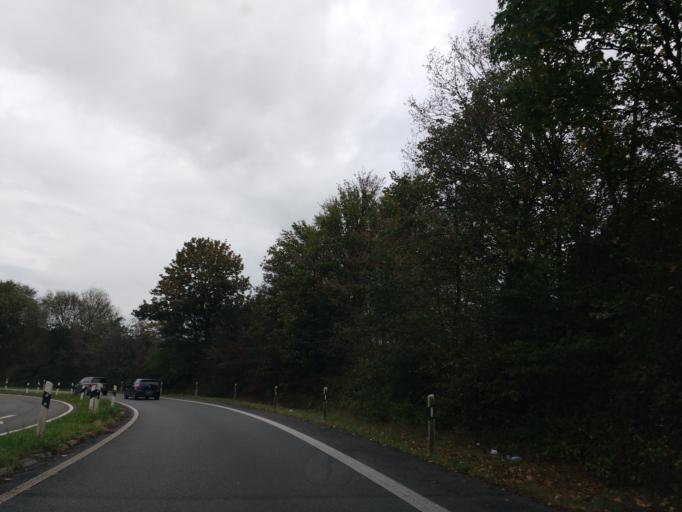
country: DE
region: North Rhine-Westphalia
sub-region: Regierungsbezirk Dusseldorf
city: Alpen
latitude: 51.5636
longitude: 6.4901
